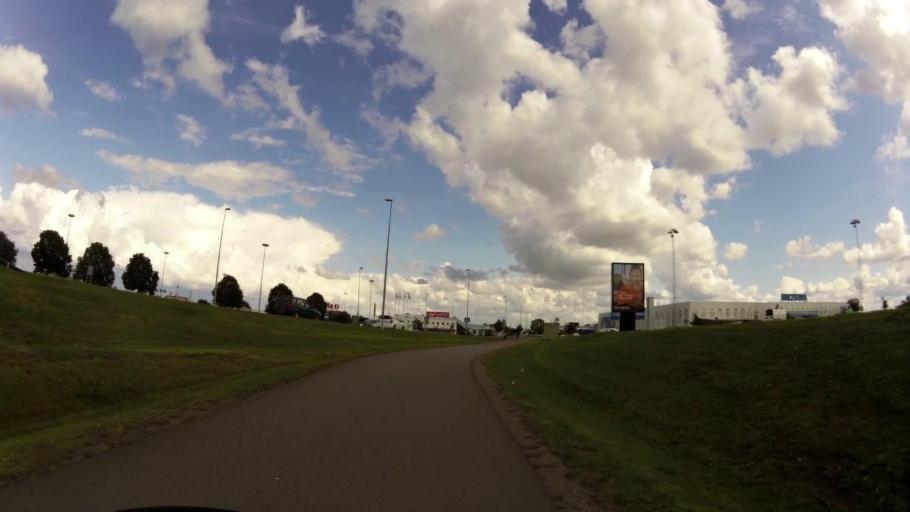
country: SE
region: OEstergoetland
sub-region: Linkopings Kommun
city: Linkoping
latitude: 58.4305
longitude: 15.5869
